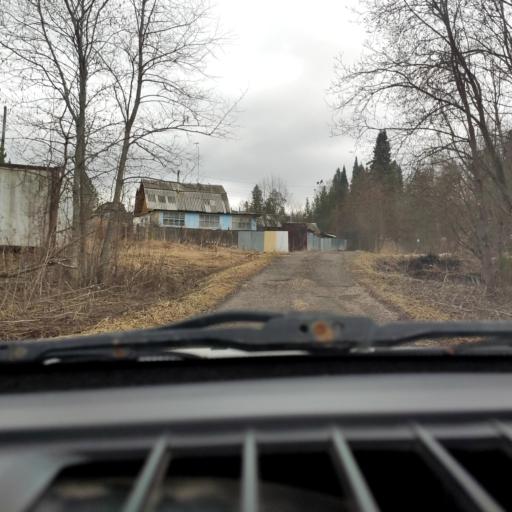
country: RU
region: Perm
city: Kultayevo
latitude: 57.8263
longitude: 55.7853
